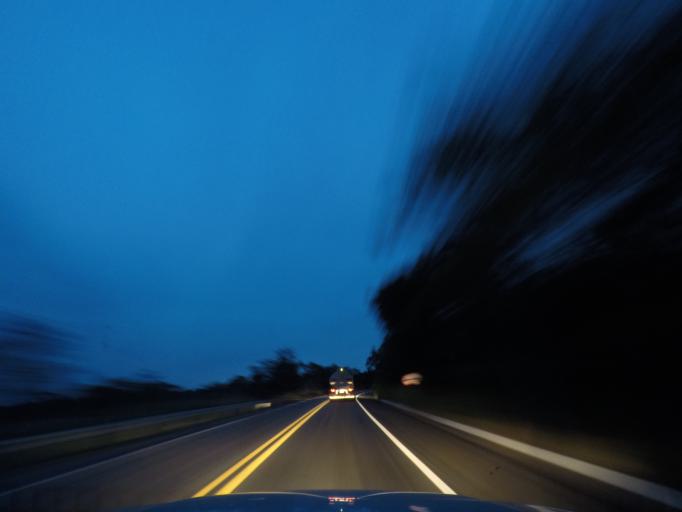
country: BR
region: Bahia
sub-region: Andarai
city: Vera Cruz
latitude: -12.4984
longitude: -41.3291
